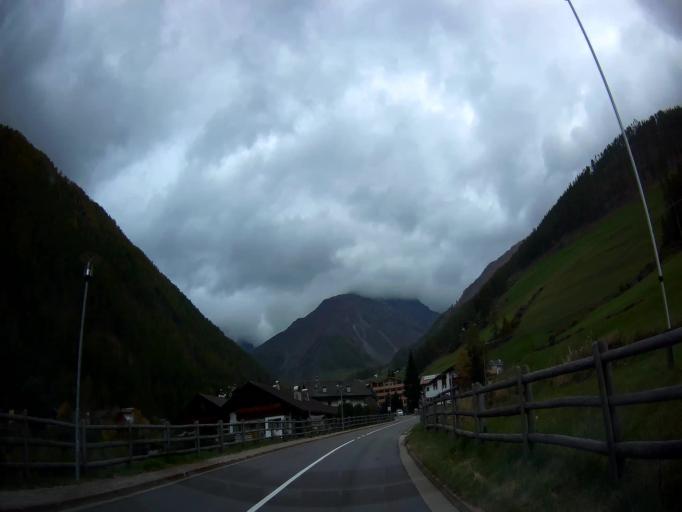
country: IT
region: Trentino-Alto Adige
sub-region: Bolzano
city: Senales
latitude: 46.7240
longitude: 10.8594
